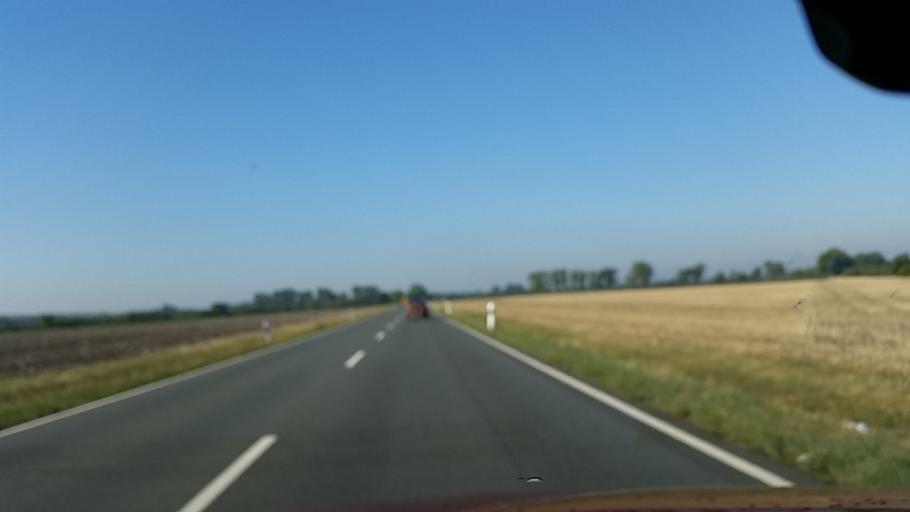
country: DE
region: Thuringia
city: Kolleda
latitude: 51.1772
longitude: 11.2159
